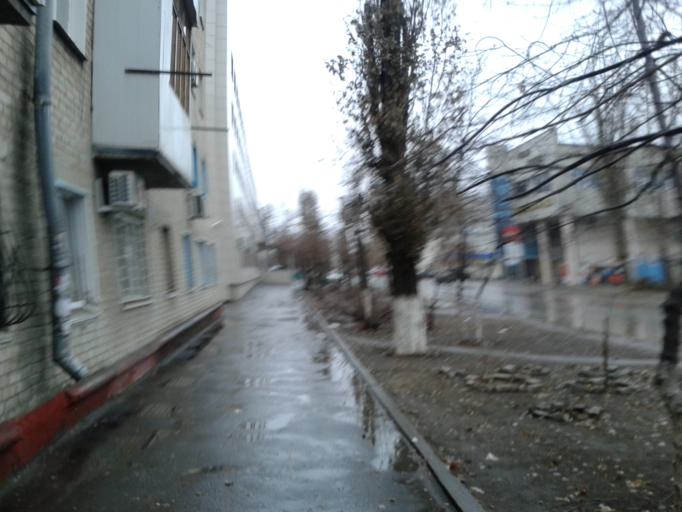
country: RU
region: Volgograd
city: Volgograd
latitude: 48.6934
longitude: 44.4881
